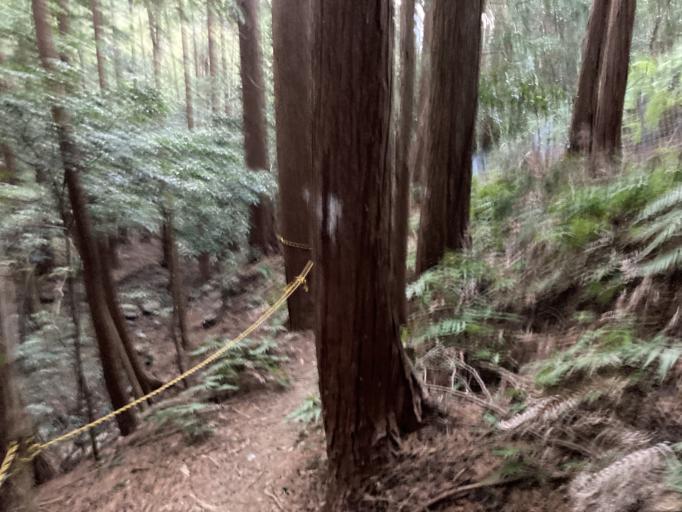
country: JP
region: Aichi
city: Tahara
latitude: 34.6078
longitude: 137.1471
